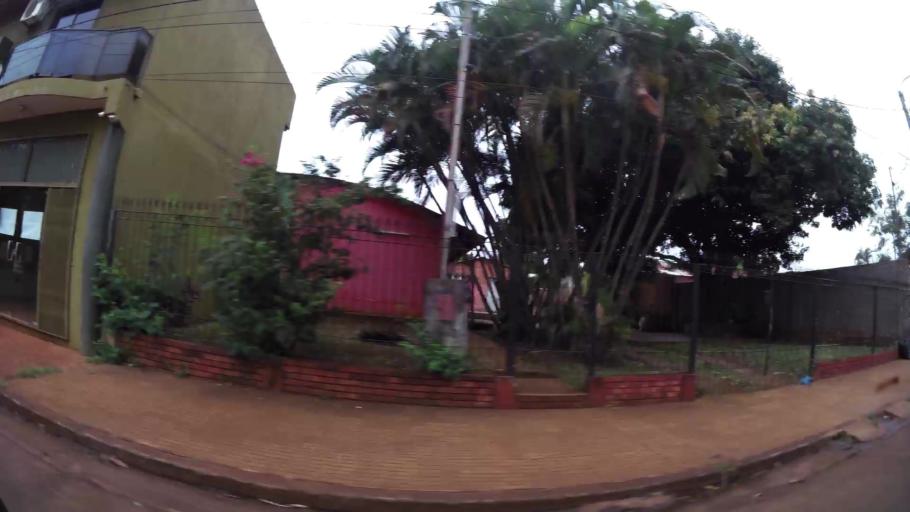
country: PY
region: Alto Parana
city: Ciudad del Este
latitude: -25.4040
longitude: -54.6275
